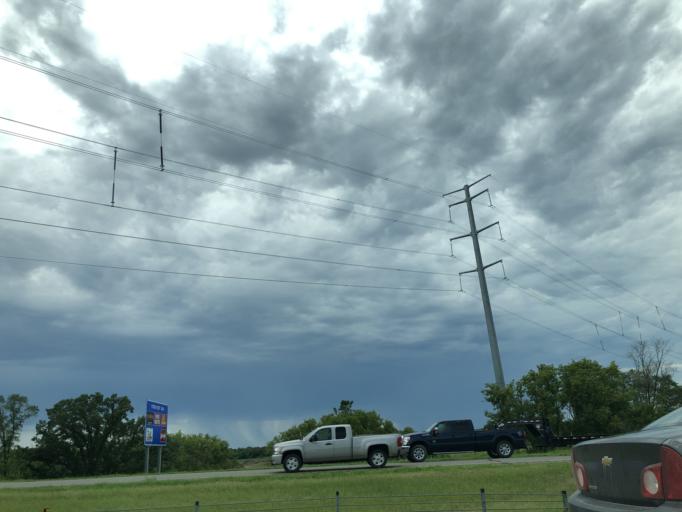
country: US
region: Minnesota
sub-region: Stearns County
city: Saint Joseph
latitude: 45.5231
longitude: -94.2971
